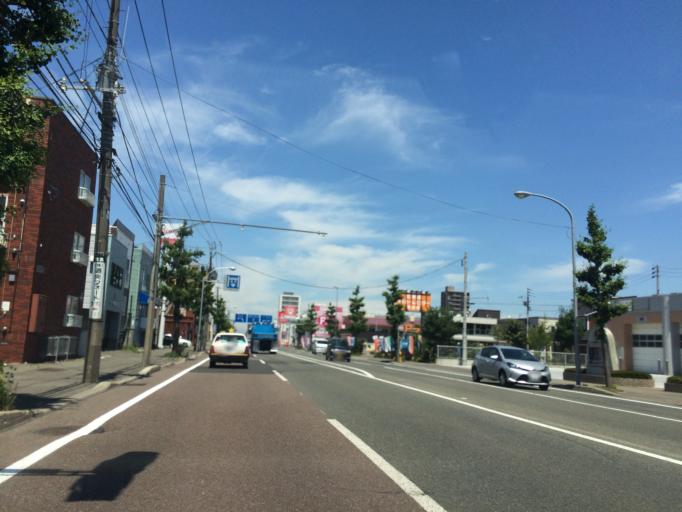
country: JP
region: Hokkaido
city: Sapporo
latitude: 43.0280
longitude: 141.3452
